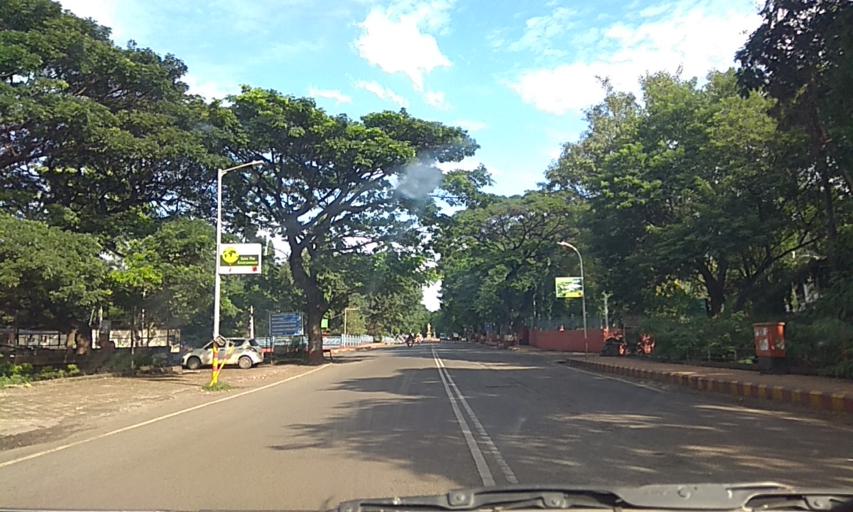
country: IN
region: Maharashtra
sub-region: Pune Division
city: Pune
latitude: 18.5241
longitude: 73.8811
